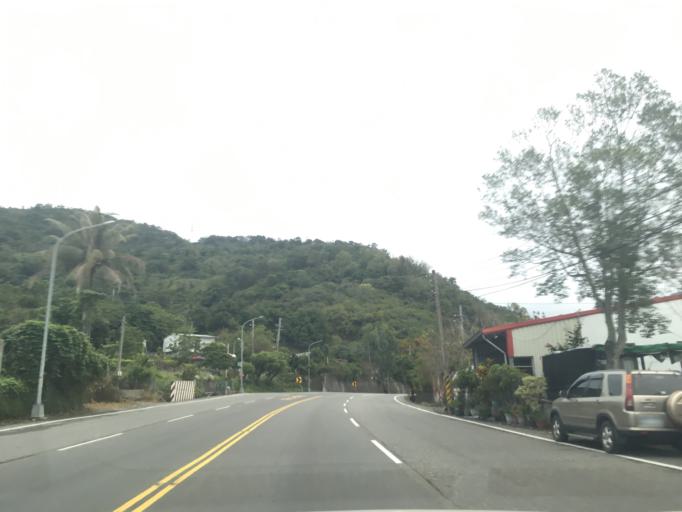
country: TW
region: Taiwan
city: Taitung City
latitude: 22.7486
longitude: 121.0553
